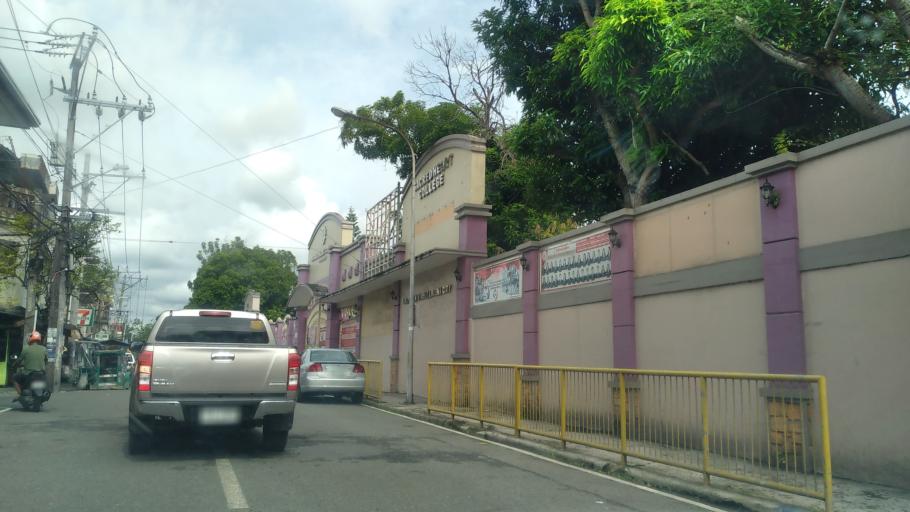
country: PH
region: Calabarzon
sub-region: Province of Quezon
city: Lucena
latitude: 13.9396
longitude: 121.6146
